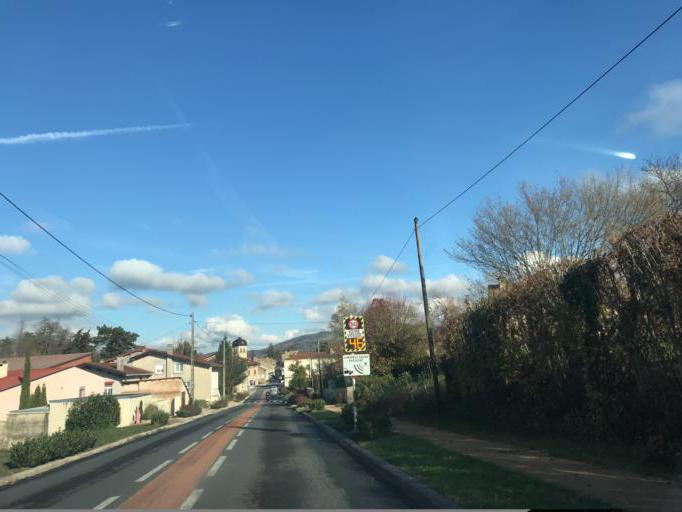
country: FR
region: Rhone-Alpes
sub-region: Departement de l'Ain
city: Saint-Jean-le-Vieux
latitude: 46.0260
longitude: 5.3851
